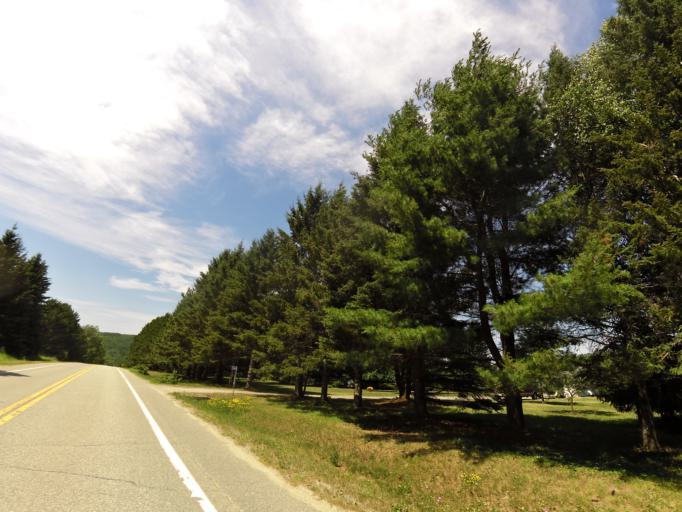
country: CA
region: Quebec
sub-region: Abitibi-Temiscamingue
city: Ville-Marie
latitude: 47.2946
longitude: -79.4287
